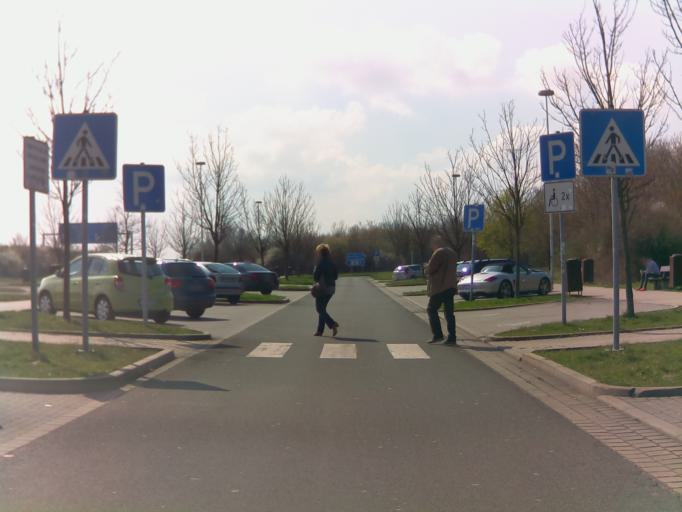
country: DE
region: Saxony-Anhalt
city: Stossen
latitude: 51.1055
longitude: 11.9548
